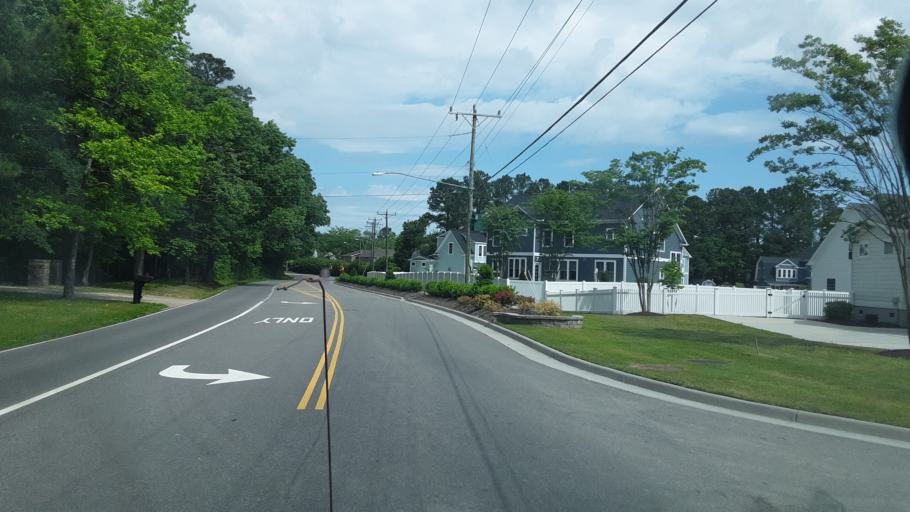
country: US
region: Virginia
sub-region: City of Virginia Beach
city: Virginia Beach
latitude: 36.7414
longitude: -75.9887
